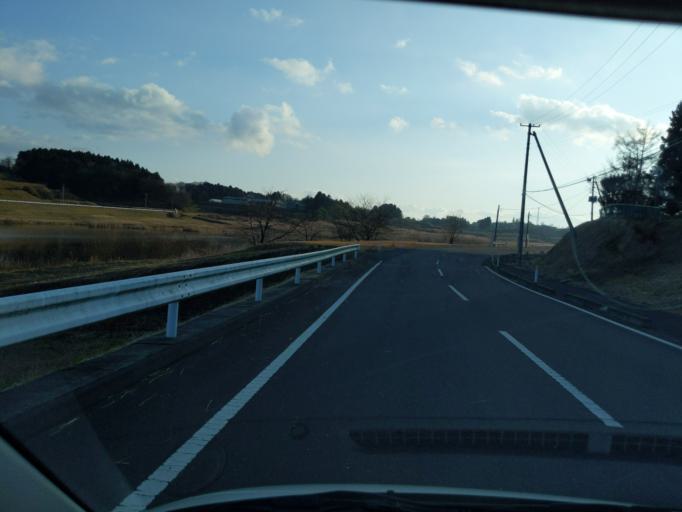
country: JP
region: Miyagi
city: Wakuya
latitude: 38.6820
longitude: 141.1119
